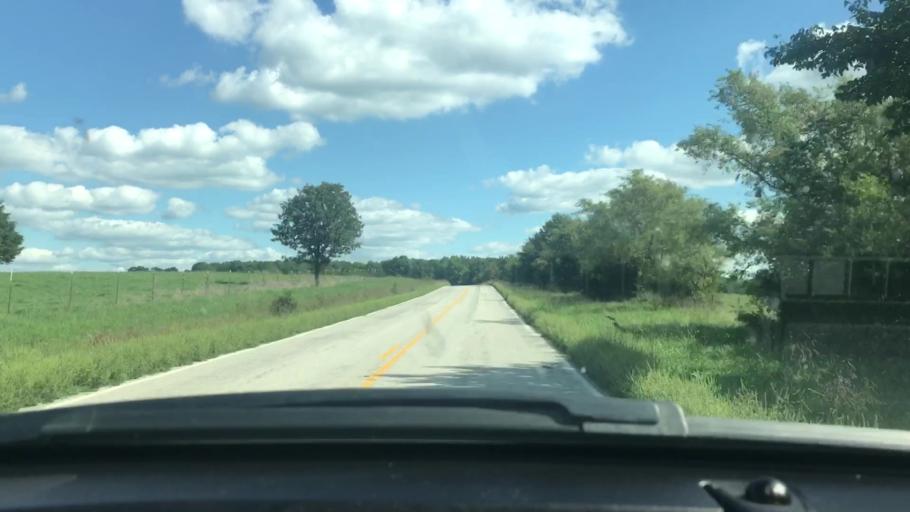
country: US
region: Missouri
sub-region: Wright County
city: Hartville
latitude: 37.3799
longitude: -92.4362
